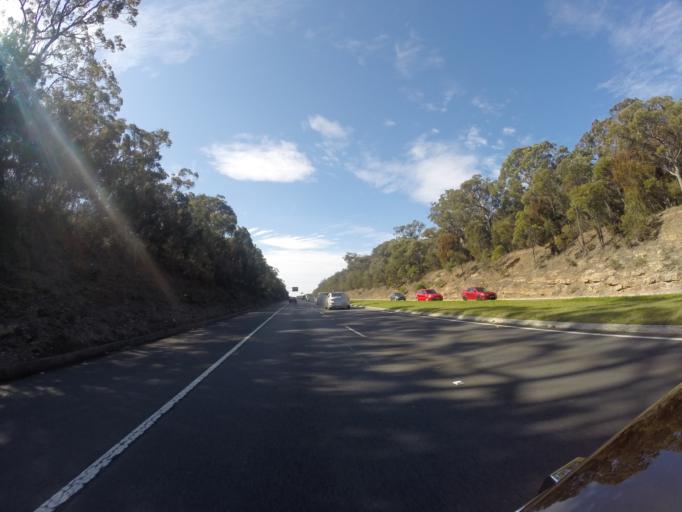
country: AU
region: New South Wales
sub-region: Sutherland Shire
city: Loftus
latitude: -34.0551
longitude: 151.0437
